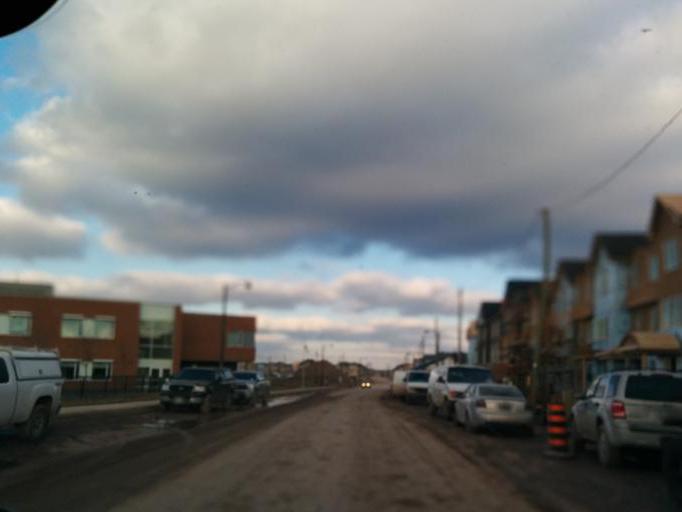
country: CA
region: Ontario
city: Oakville
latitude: 43.4709
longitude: -79.7439
